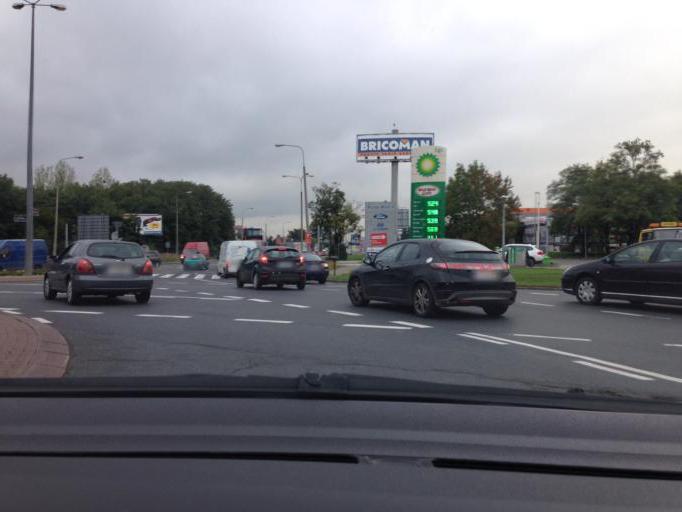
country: PL
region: Greater Poland Voivodeship
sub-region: Poznan
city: Poznan
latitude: 52.4432
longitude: 16.9096
